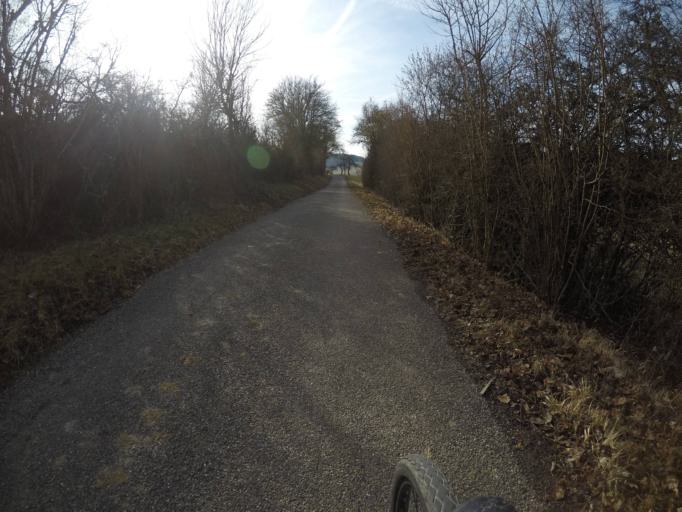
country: DE
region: Baden-Wuerttemberg
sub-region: Karlsruhe Region
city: Wildberg
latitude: 48.6377
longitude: 8.7670
